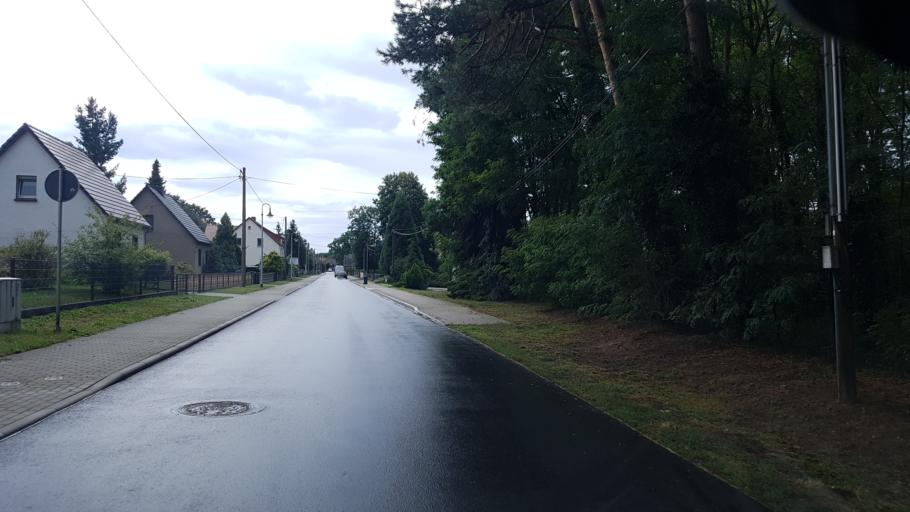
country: DE
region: Saxony
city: Gross Duben
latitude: 51.6276
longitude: 14.5435
